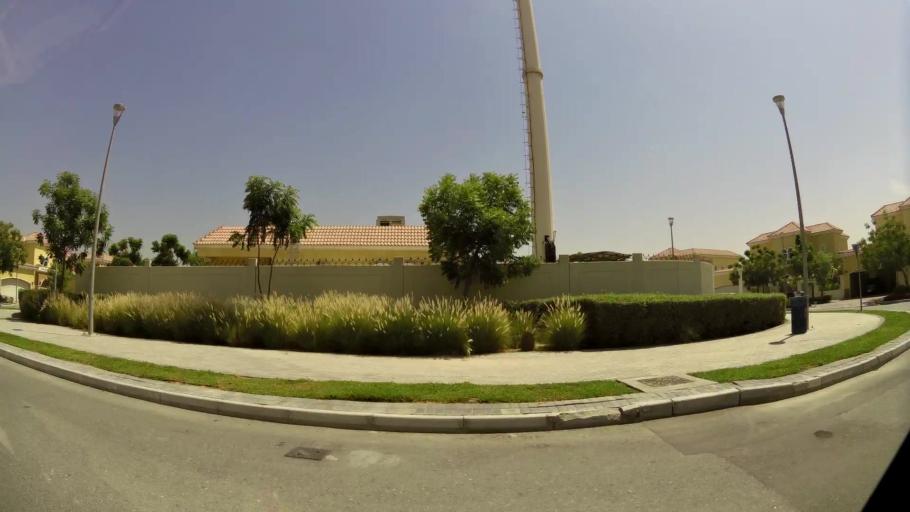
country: AE
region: Dubai
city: Dubai
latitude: 25.0399
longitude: 55.1618
